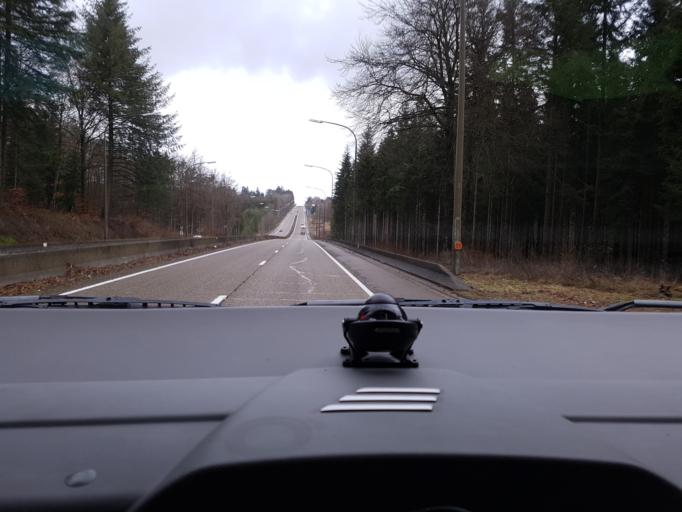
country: BE
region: Wallonia
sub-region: Province du Luxembourg
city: Tenneville
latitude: 50.0970
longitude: 5.4834
